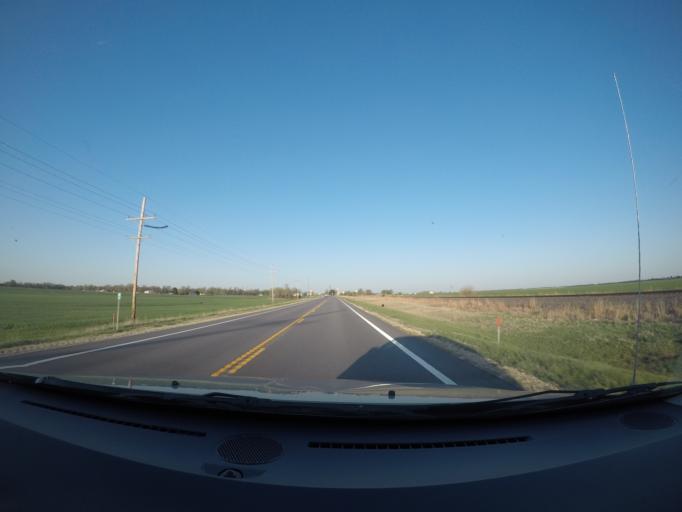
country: US
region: Kansas
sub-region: Stafford County
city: Stafford
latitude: 37.8147
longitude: -98.4205
